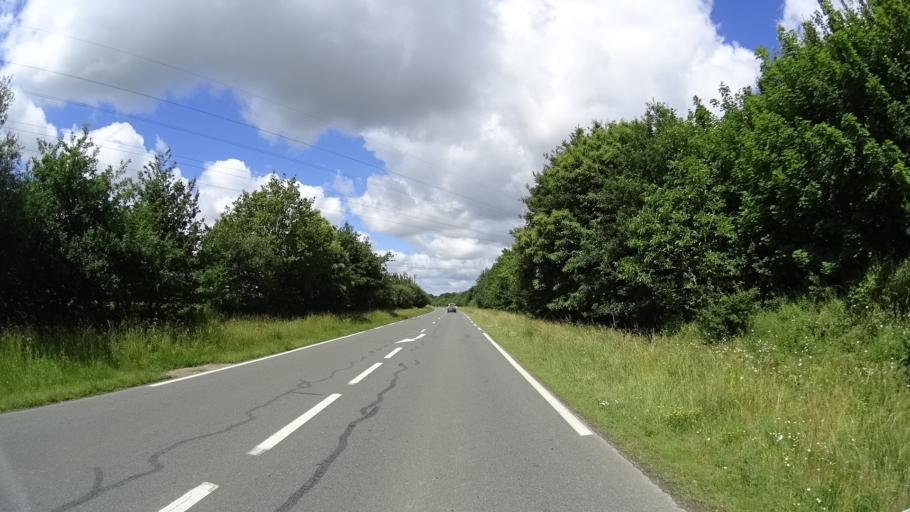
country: FR
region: Brittany
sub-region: Departement d'Ille-et-Vilaine
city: Le Rheu
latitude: 48.1169
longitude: -1.8106
